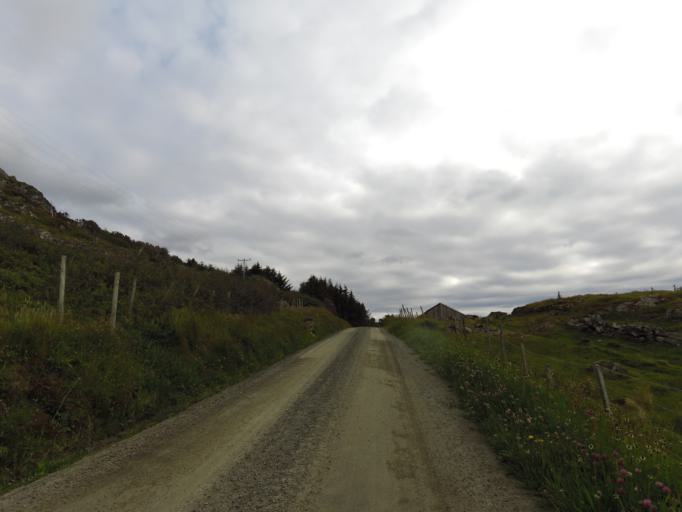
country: NO
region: Vest-Agder
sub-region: Farsund
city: Vestbygd
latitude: 58.1445
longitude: 6.6134
